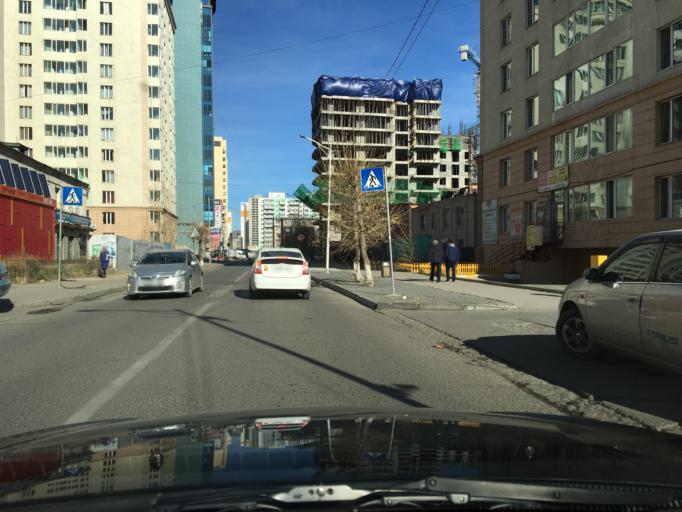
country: MN
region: Ulaanbaatar
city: Ulaanbaatar
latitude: 47.8973
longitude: 106.8962
